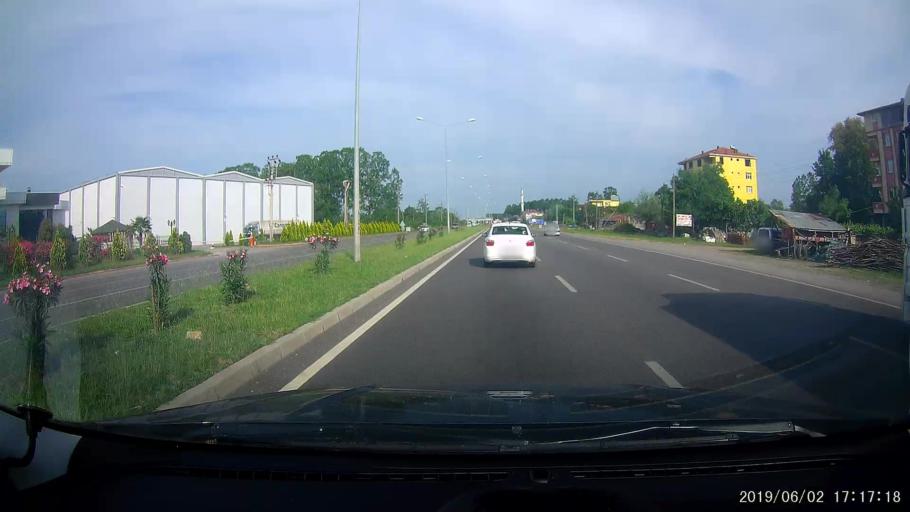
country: TR
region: Samsun
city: Dikbiyik
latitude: 41.2299
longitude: 36.5792
